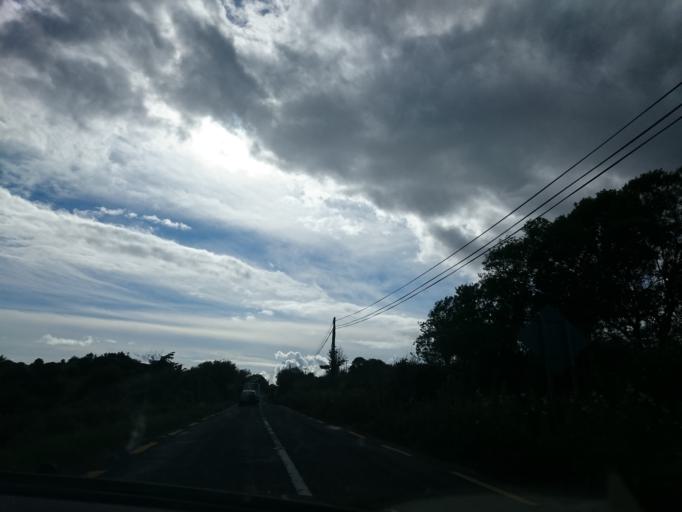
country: IE
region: Connaught
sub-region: Maigh Eo
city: Westport
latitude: 53.9032
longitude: -9.5792
